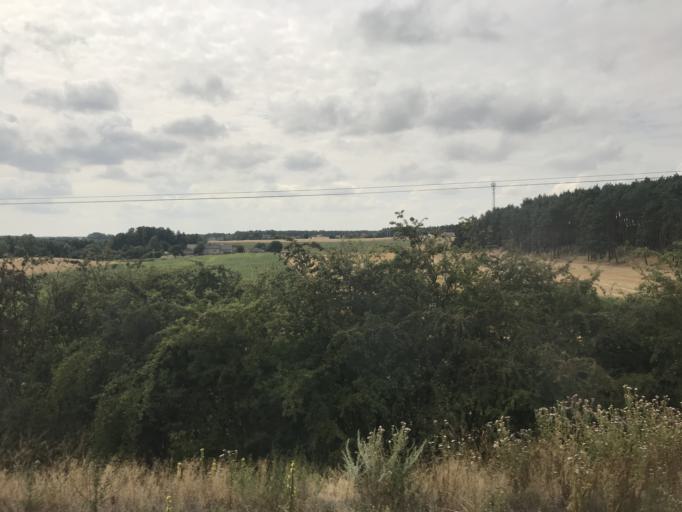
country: PL
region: Greater Poland Voivodeship
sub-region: Powiat gnieznienski
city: Niechanowo
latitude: 52.5351
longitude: 17.7021
